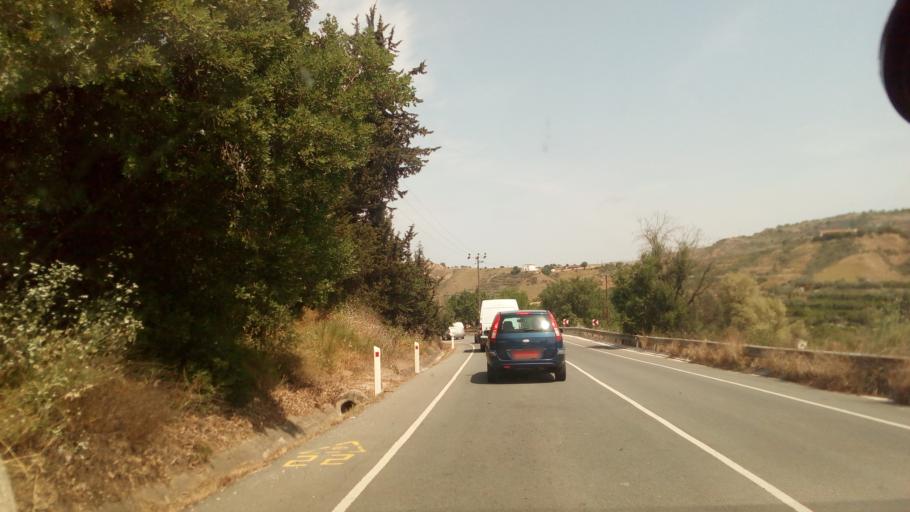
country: CY
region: Pafos
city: Tala
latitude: 34.9298
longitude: 32.4762
